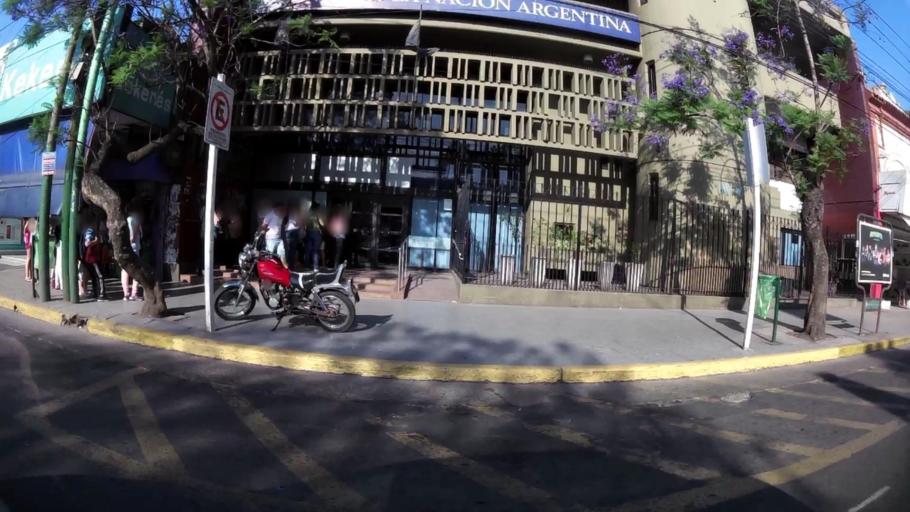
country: AR
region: Buenos Aires
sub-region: Partido de Merlo
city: Merlo
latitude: -34.6697
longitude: -58.7254
